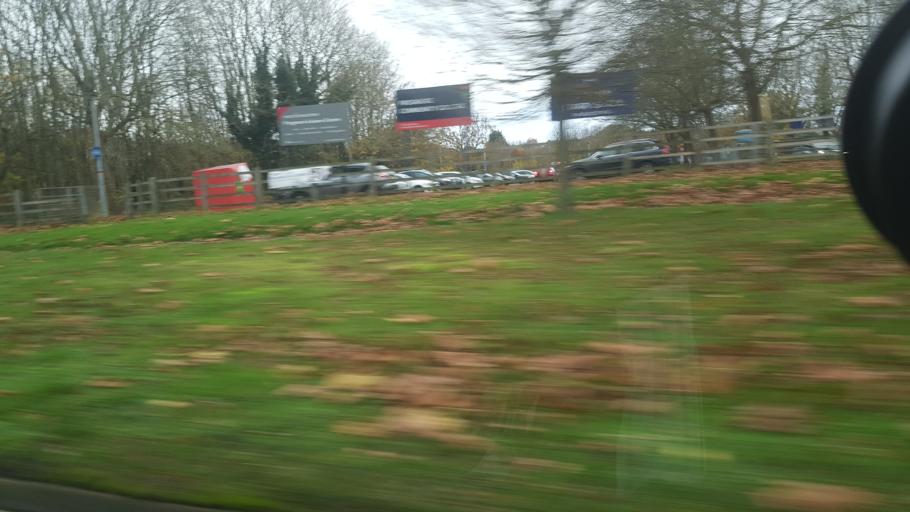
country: GB
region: England
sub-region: Hampshire
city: Yateley
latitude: 51.3369
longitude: -0.8078
